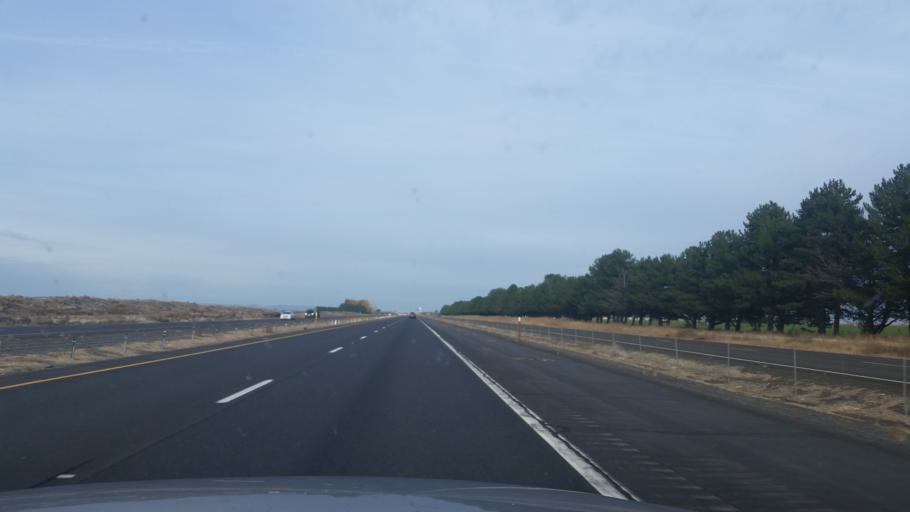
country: US
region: Washington
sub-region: Grant County
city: Quincy
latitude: 47.0622
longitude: -119.8896
